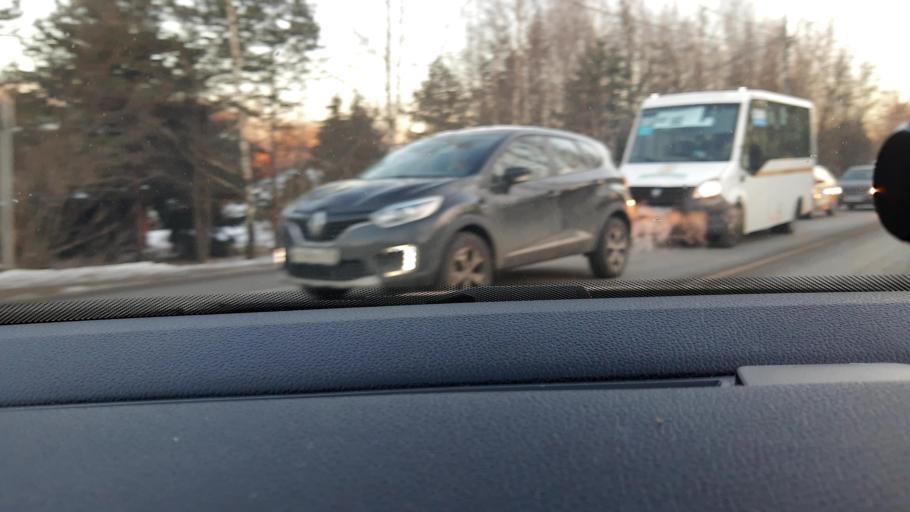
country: RU
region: Moskovskaya
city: Pirogovskiy
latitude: 55.9638
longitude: 37.7449
